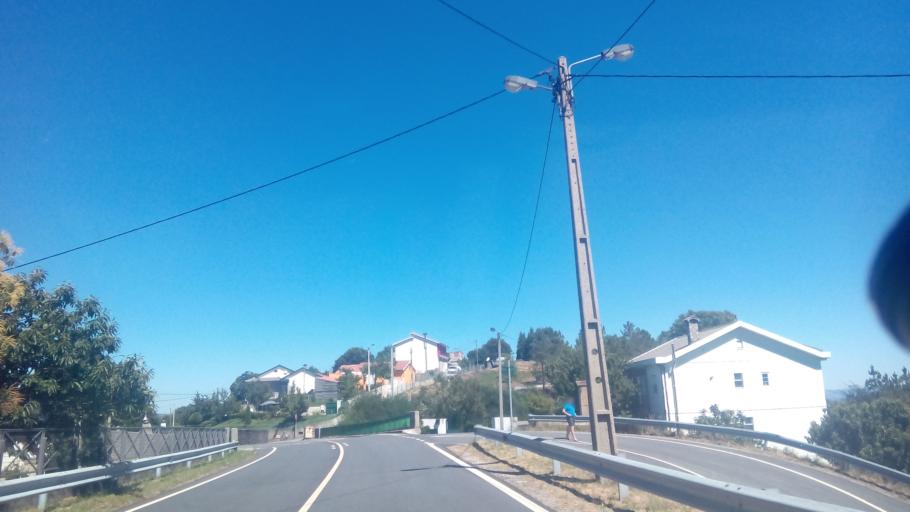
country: PT
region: Vila Real
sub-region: Santa Marta de Penaguiao
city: Santa Marta de Penaguiao
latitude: 41.2804
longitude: -7.8669
